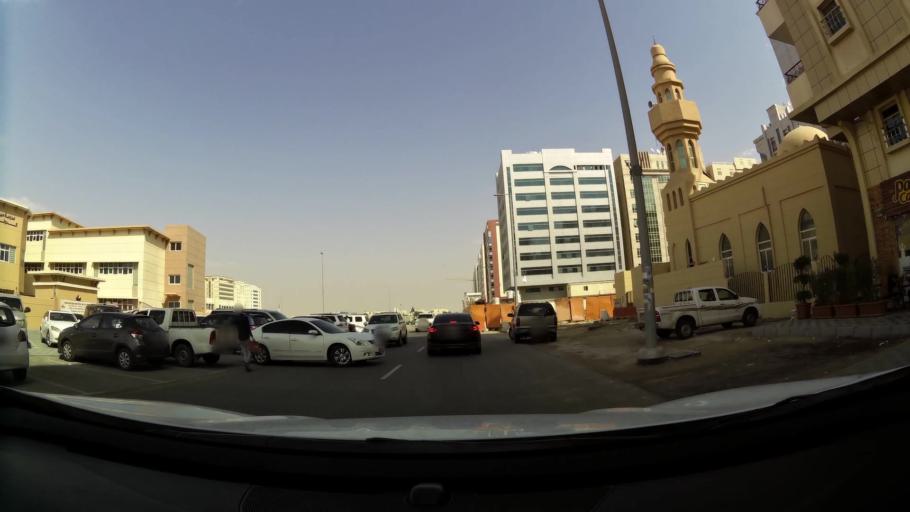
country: AE
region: Abu Dhabi
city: Abu Dhabi
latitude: 24.3416
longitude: 54.5331
